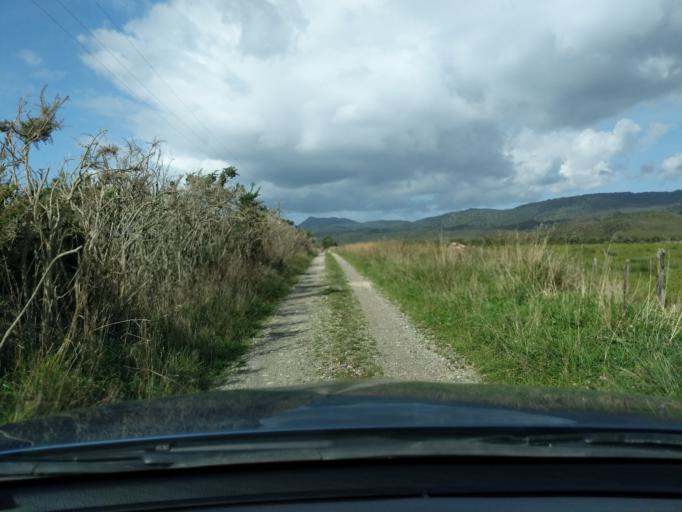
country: NZ
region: Tasman
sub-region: Tasman District
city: Takaka
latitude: -40.6517
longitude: 172.4728
